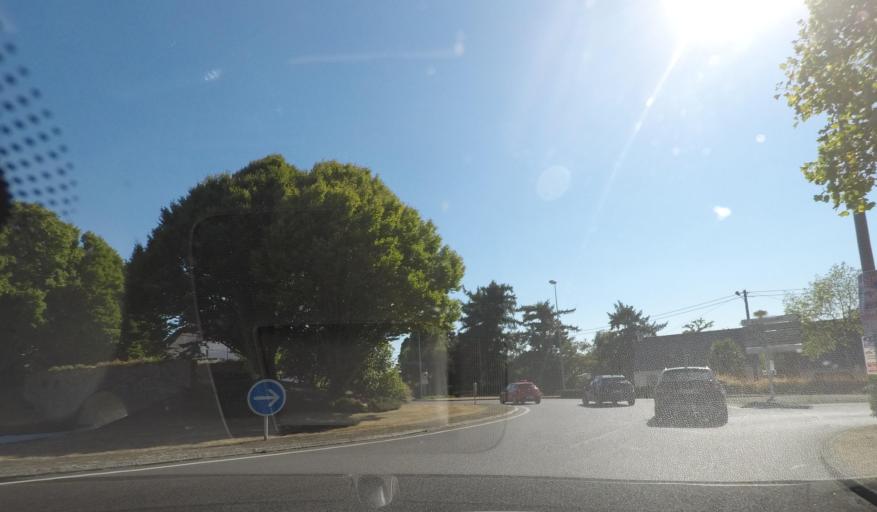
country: FR
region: Pays de la Loire
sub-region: Departement de la Loire-Atlantique
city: Pontchateau
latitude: 47.4324
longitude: -2.0840
